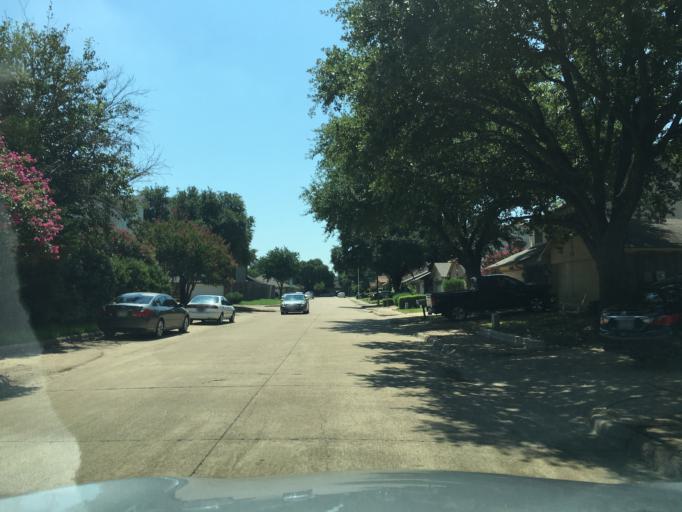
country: US
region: Texas
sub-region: Dallas County
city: Garland
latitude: 32.9501
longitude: -96.6692
